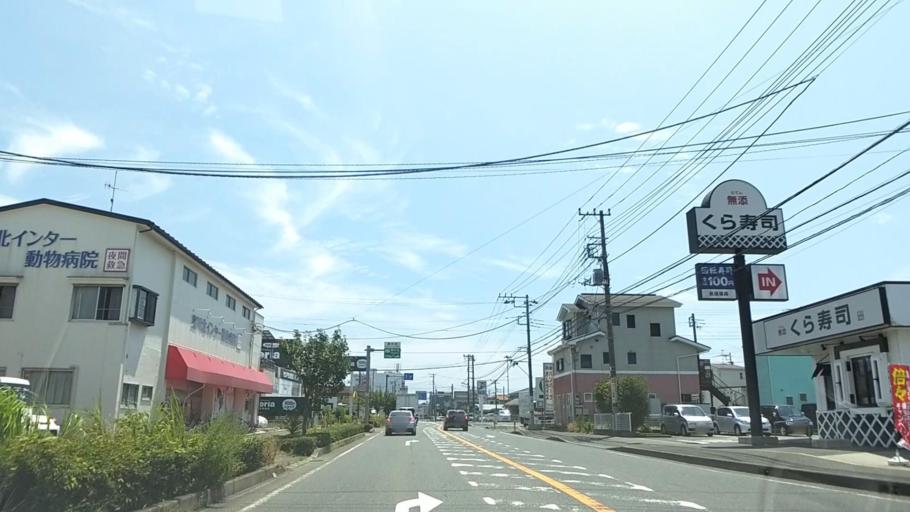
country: JP
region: Kanagawa
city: Atsugi
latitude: 35.3919
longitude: 139.3801
